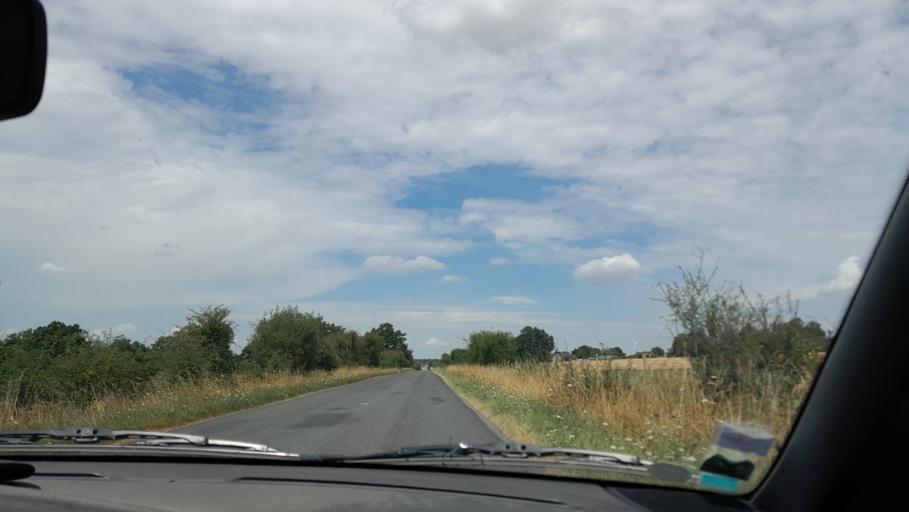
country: FR
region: Pays de la Loire
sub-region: Departement de la Mayenne
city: Saint-Pierre-la-Cour
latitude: 48.0985
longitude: -1.0187
